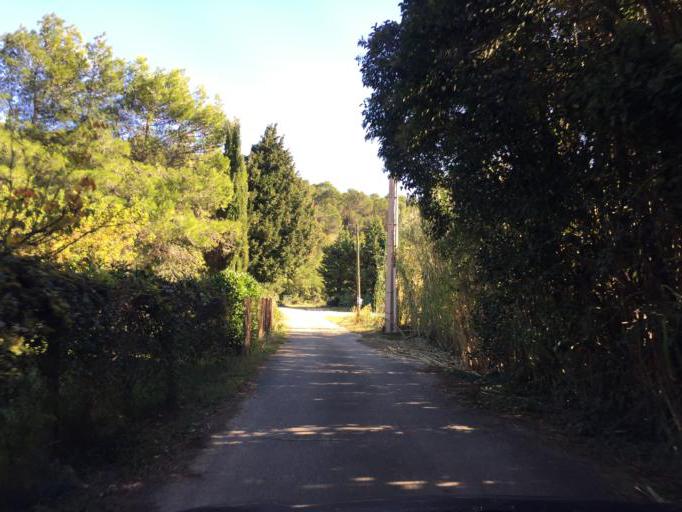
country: FR
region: Provence-Alpes-Cote d'Azur
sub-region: Departement du Vaucluse
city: Piolenc
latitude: 44.1907
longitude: 4.7517
